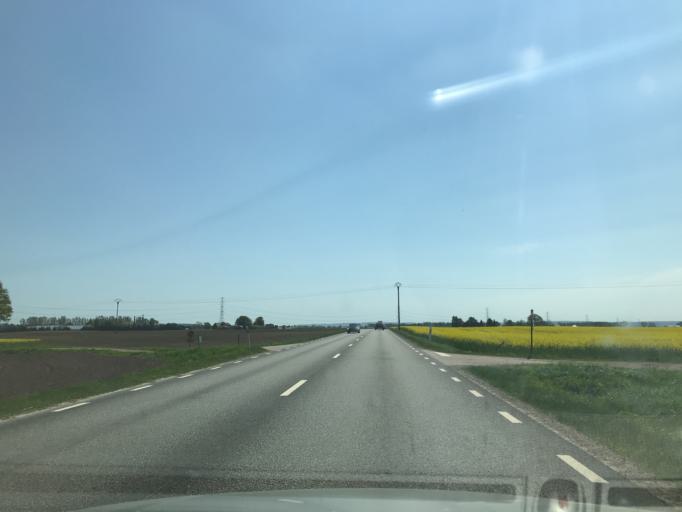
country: SE
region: Skane
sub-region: Astorps Kommun
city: Kvidinge
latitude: 56.2027
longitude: 13.0443
